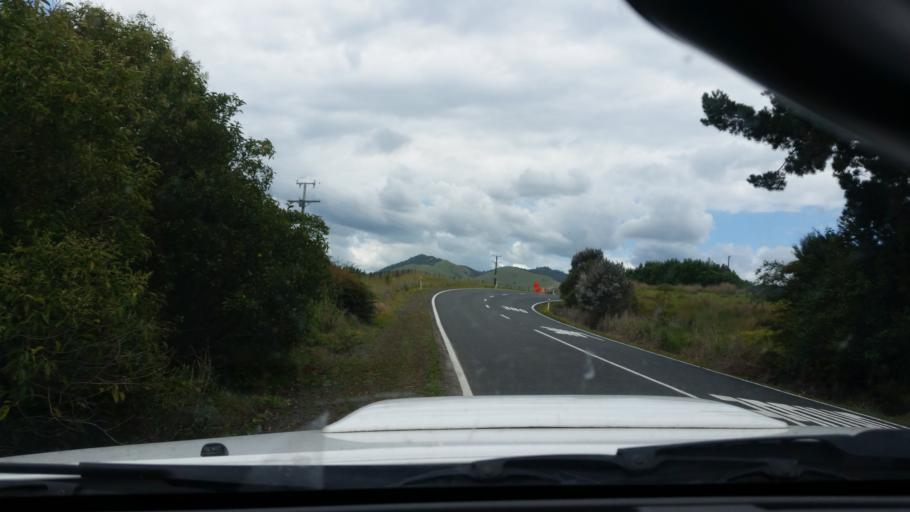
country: NZ
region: Northland
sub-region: Kaipara District
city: Dargaville
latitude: -35.7497
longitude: 173.8852
